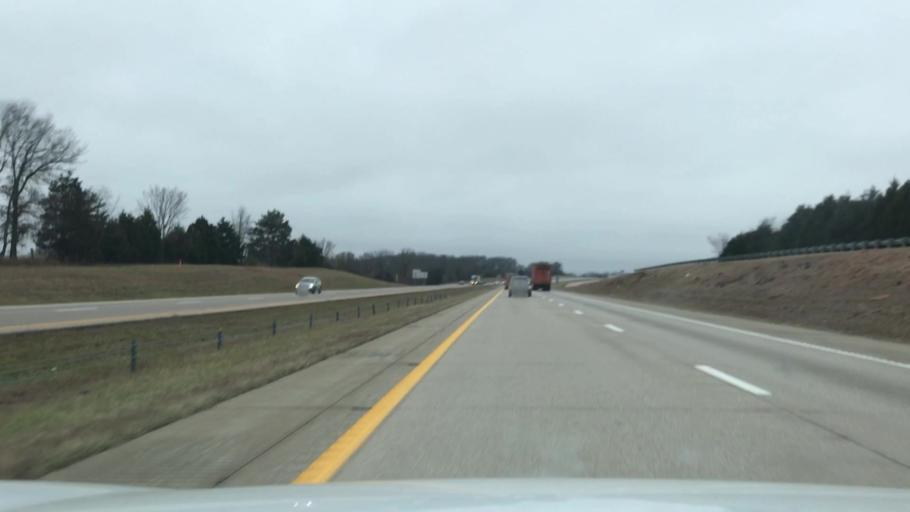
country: US
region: Missouri
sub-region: Crawford County
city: Bourbon
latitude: 38.1431
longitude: -91.2687
